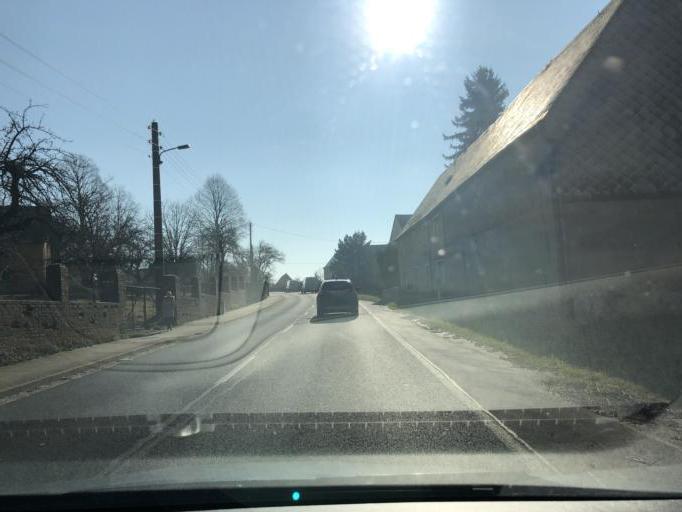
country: DE
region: Saxony
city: Bischofswerda
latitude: 51.1454
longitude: 14.1623
